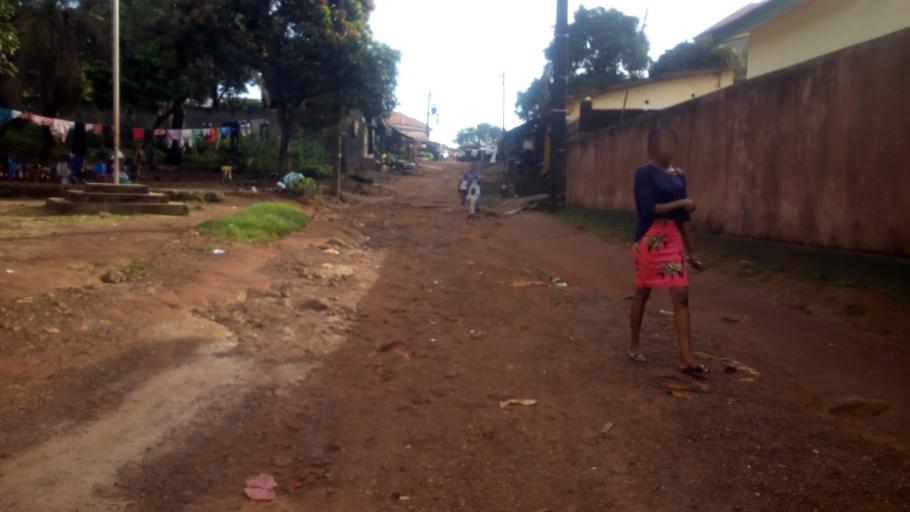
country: GN
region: Conakry
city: Conakry
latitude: 9.6240
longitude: -13.6113
